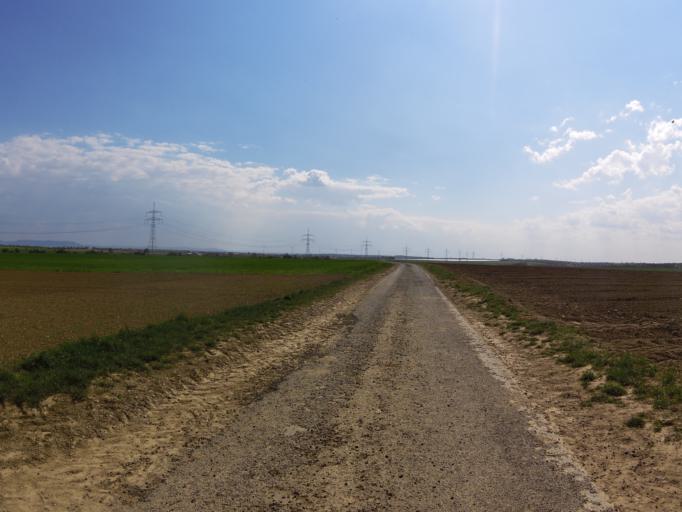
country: DE
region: Bavaria
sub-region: Regierungsbezirk Unterfranken
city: Oberpleichfeld
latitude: 49.8481
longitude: 10.0879
